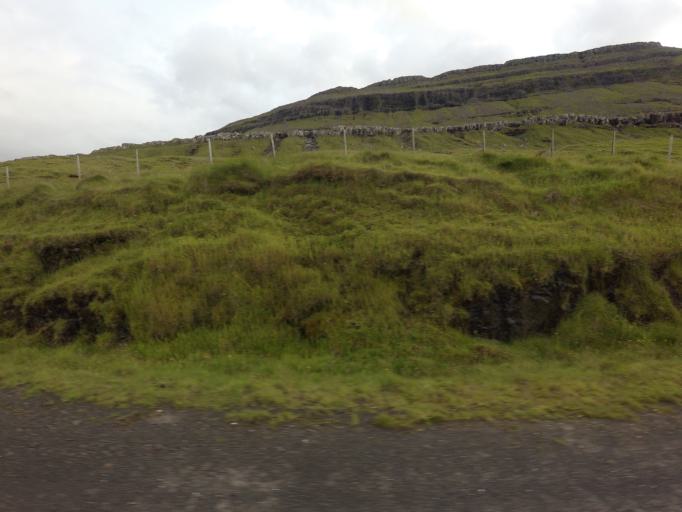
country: FO
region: Streymoy
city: Kollafjordhur
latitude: 62.1406
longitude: -6.8962
